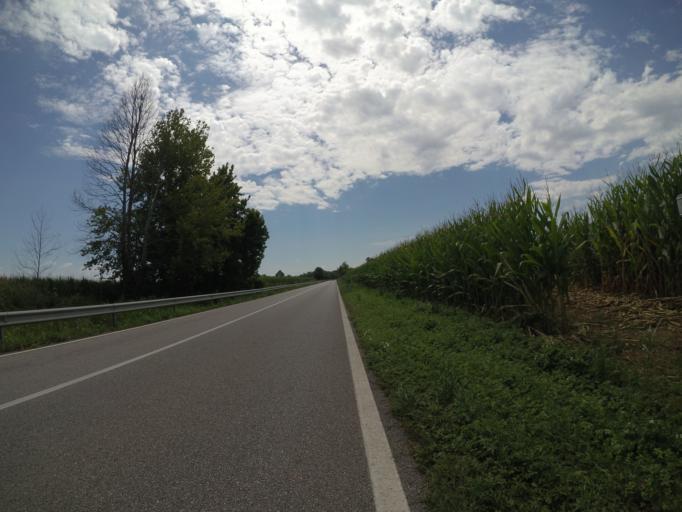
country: IT
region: Friuli Venezia Giulia
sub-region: Provincia di Udine
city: Lestizza
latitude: 45.9503
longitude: 13.1371
